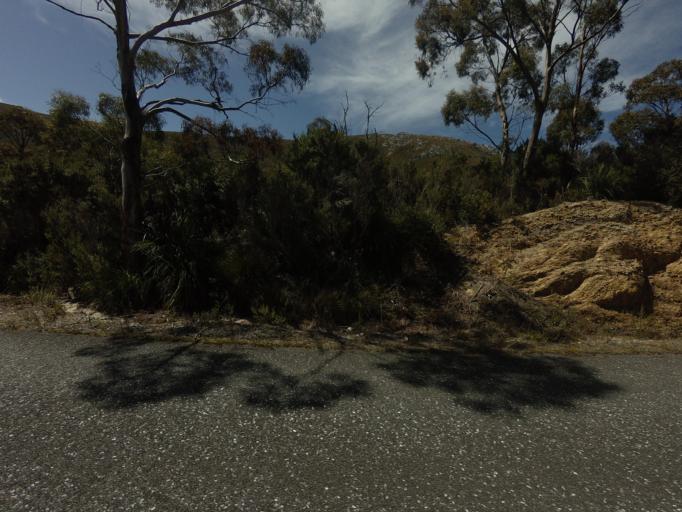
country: AU
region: Tasmania
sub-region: West Coast
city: Queenstown
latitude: -42.7909
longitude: 146.0630
